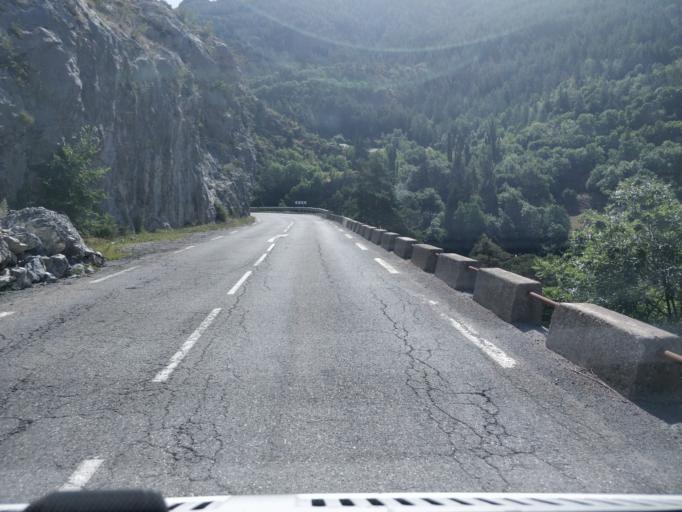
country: FR
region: Provence-Alpes-Cote d'Azur
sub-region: Departement des Alpes-de-Haute-Provence
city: Barcelonnette
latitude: 44.4003
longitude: 6.5027
